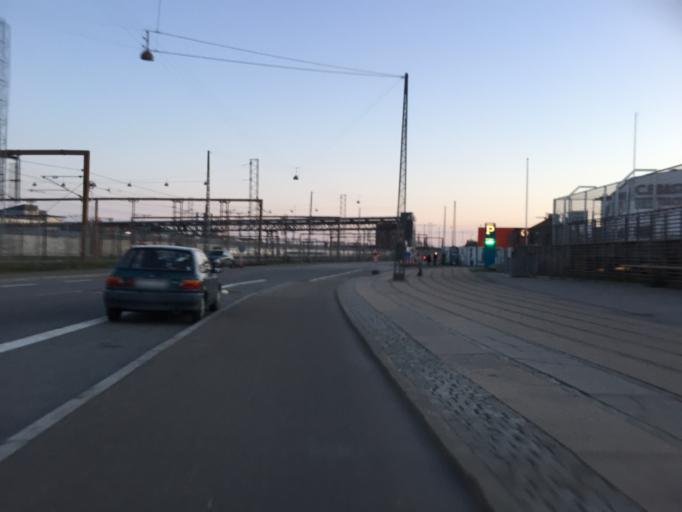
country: DK
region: Capital Region
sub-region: Kobenhavn
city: Copenhagen
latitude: 55.6681
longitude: 12.5642
